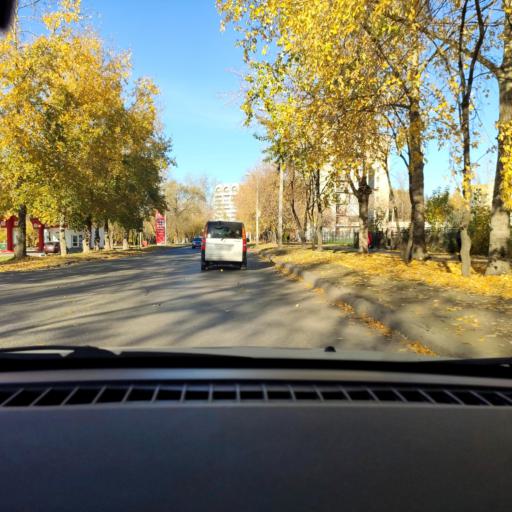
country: RU
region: Perm
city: Perm
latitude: 58.0646
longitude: 56.3544
